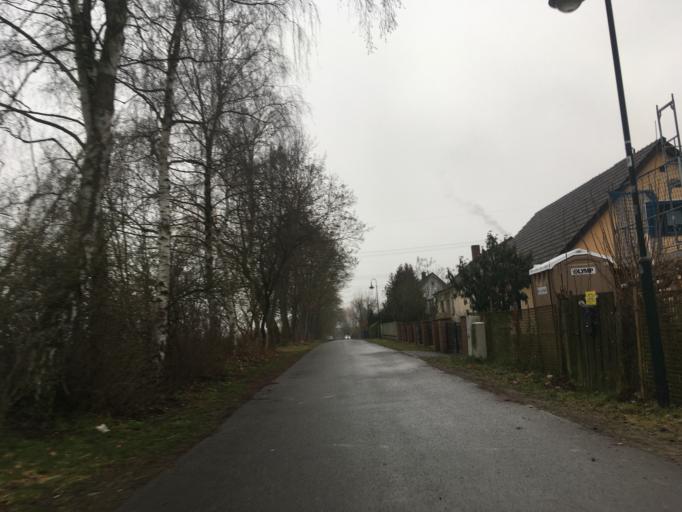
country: DE
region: Berlin
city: Buch
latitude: 52.6232
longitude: 13.5063
